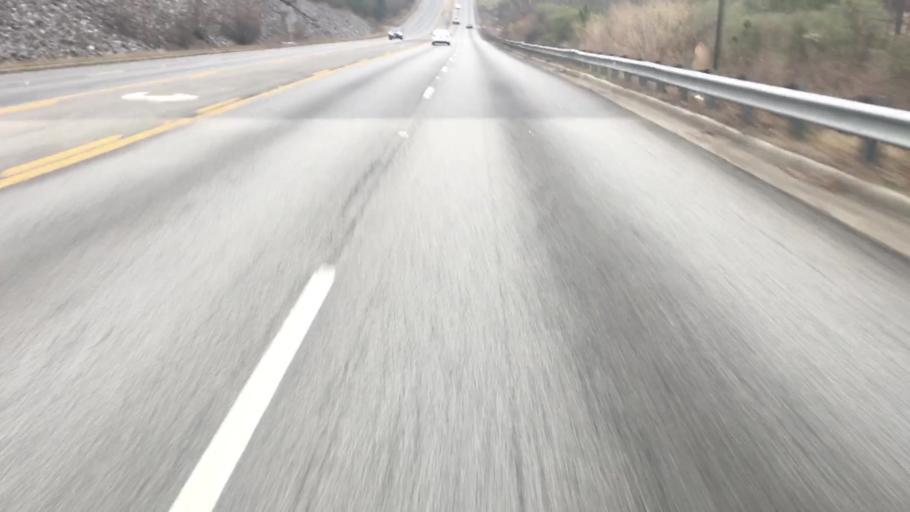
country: US
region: Alabama
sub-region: Shelby County
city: Helena
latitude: 33.3559
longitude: -86.8594
